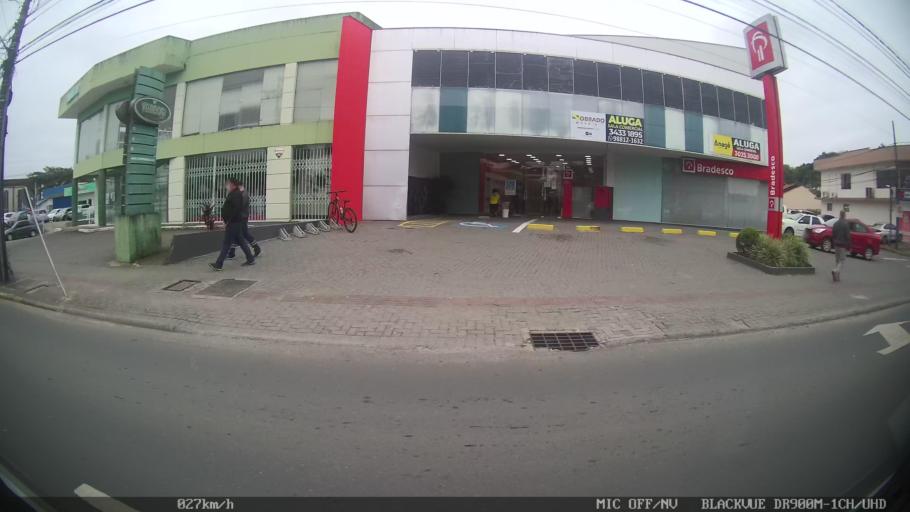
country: BR
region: Santa Catarina
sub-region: Joinville
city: Joinville
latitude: -26.3401
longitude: -48.8473
